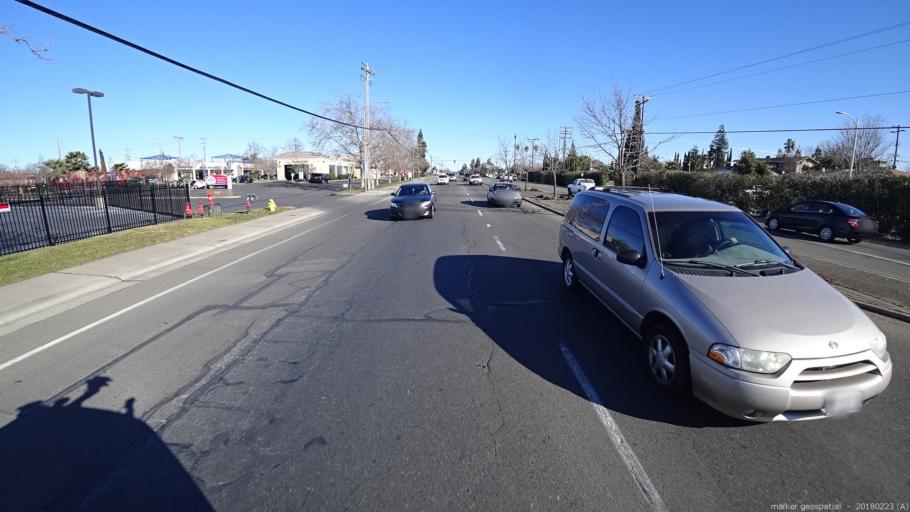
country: US
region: California
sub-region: Sacramento County
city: North Highlands
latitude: 38.6964
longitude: -121.3830
